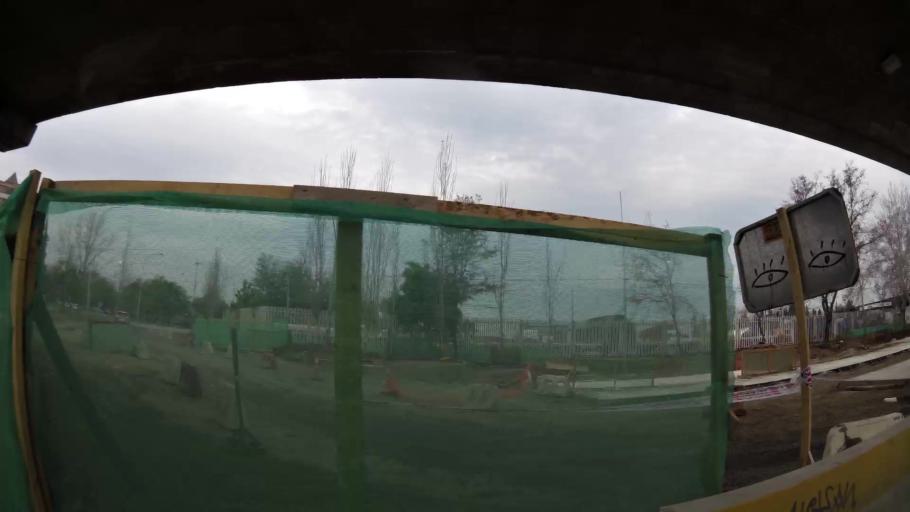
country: CL
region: Santiago Metropolitan
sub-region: Provincia de Santiago
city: Santiago
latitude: -33.4721
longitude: -70.6238
